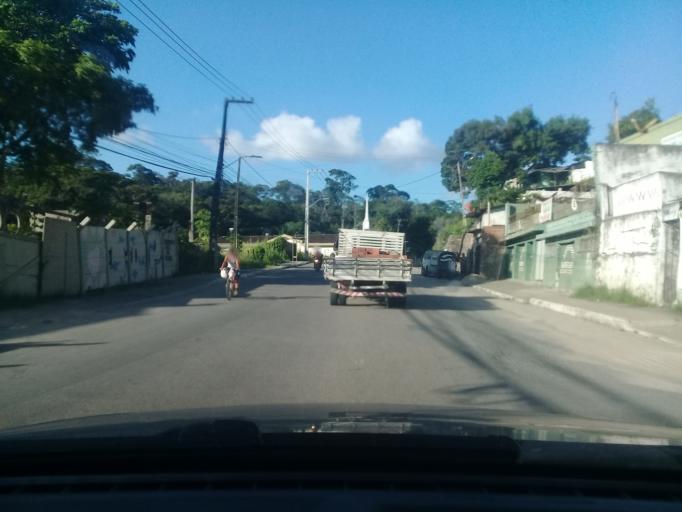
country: BR
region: Pernambuco
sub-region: Jaboatao Dos Guararapes
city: Jaboatao dos Guararapes
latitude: -8.1037
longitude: -34.9748
